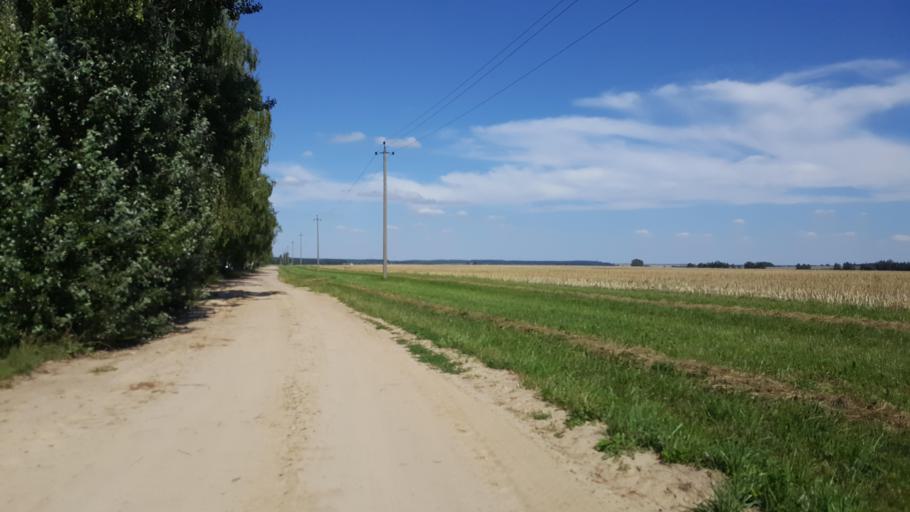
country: BY
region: Brest
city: Charnawchytsy
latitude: 52.2561
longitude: 23.5883
